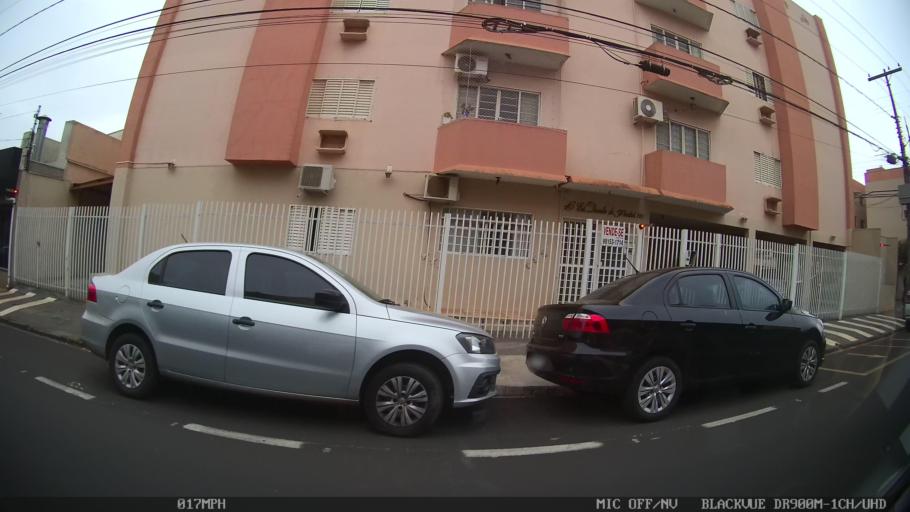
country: BR
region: Sao Paulo
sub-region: Sao Jose Do Rio Preto
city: Sao Jose do Rio Preto
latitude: -20.8376
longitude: -49.3860
